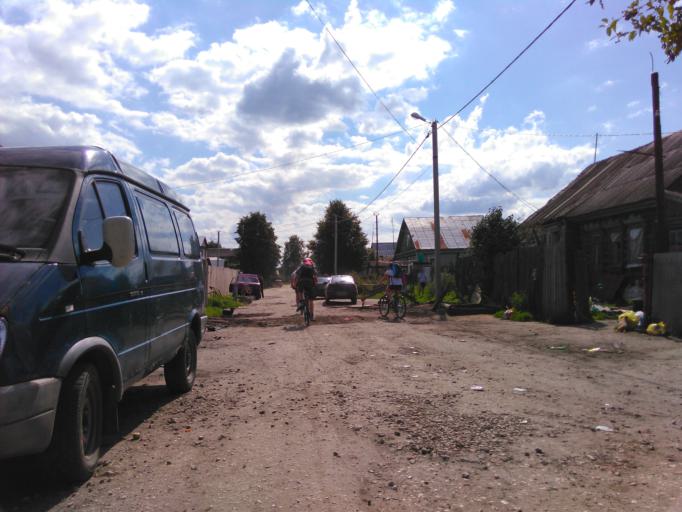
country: RU
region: Vladimir
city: Pokrov
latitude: 55.8693
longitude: 39.1065
